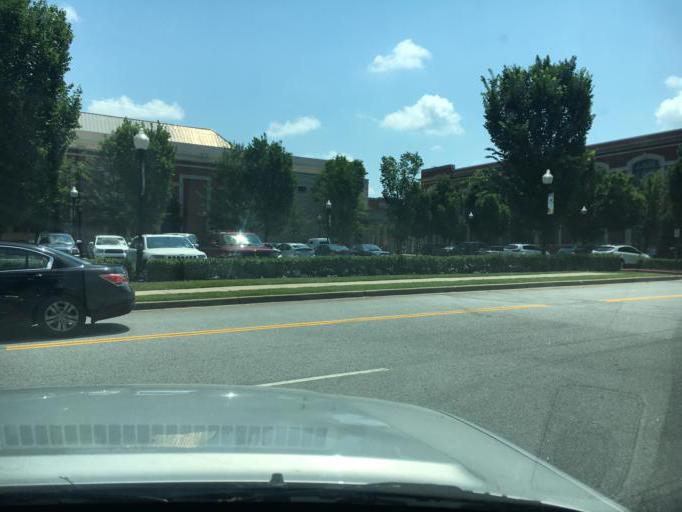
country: US
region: South Carolina
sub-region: Spartanburg County
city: Spartanburg
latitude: 34.9531
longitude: -81.9307
